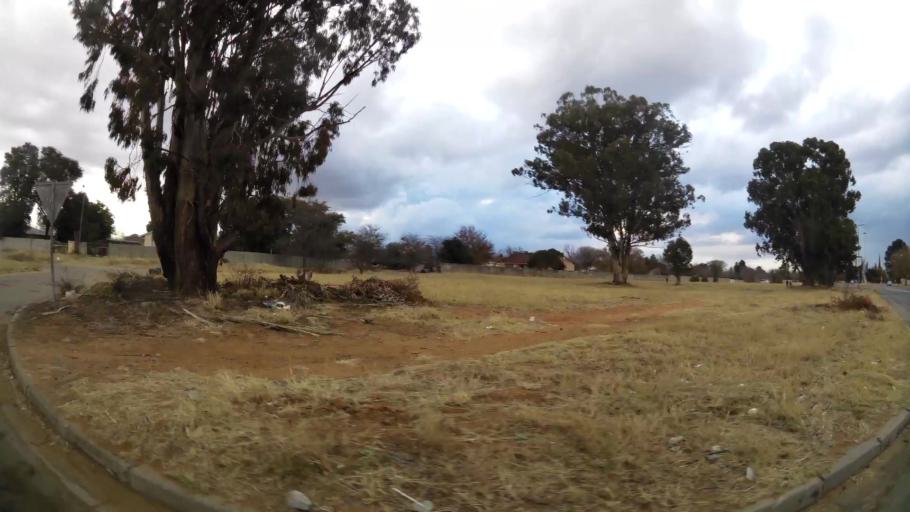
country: ZA
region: Orange Free State
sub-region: Lejweleputswa District Municipality
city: Welkom
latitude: -27.9638
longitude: 26.7258
